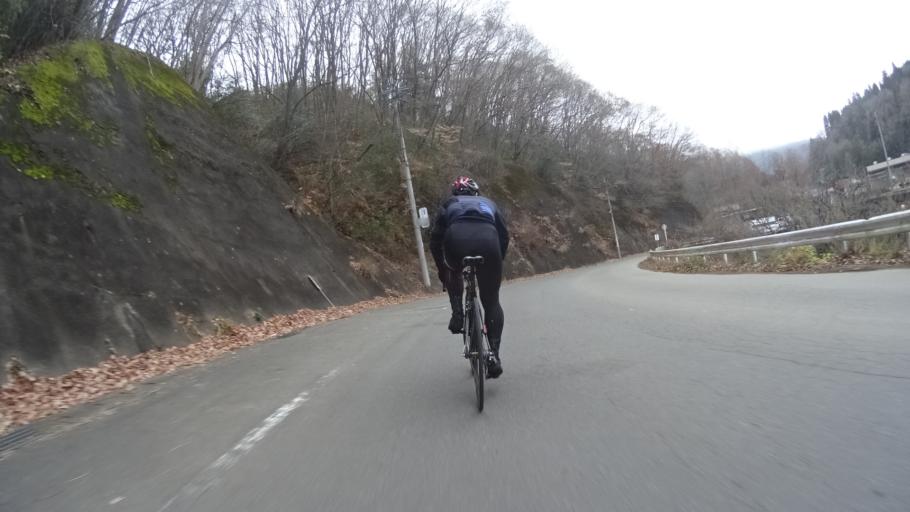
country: JP
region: Yamanashi
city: Uenohara
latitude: 35.6313
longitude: 139.1234
